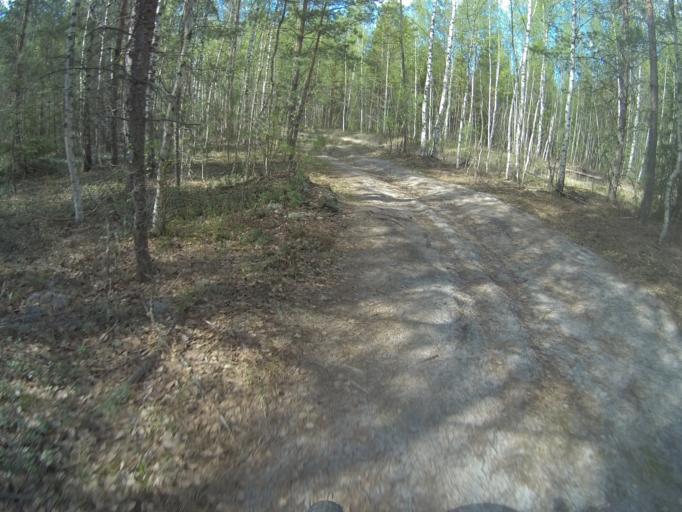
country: RU
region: Vladimir
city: Vorsha
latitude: 55.9624
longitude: 40.1957
